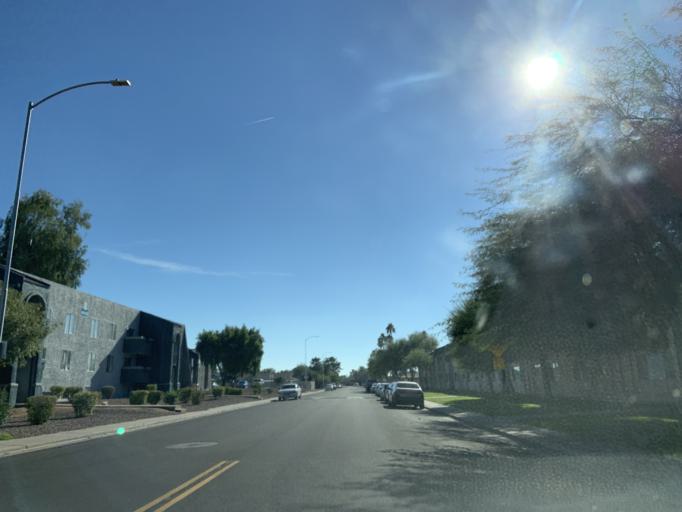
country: US
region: Arizona
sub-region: Maricopa County
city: Tempe
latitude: 33.4069
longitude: -111.8811
